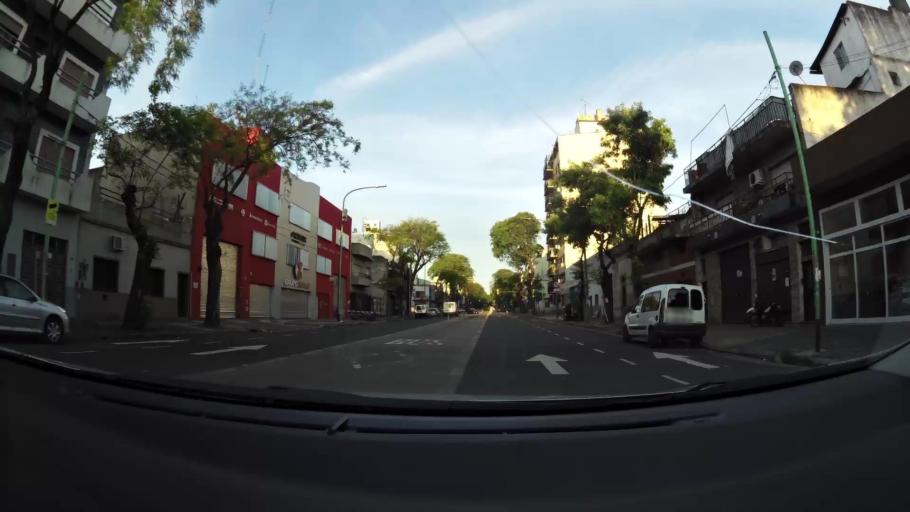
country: AR
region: Buenos Aires F.D.
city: Buenos Aires
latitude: -34.6351
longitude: -58.4103
